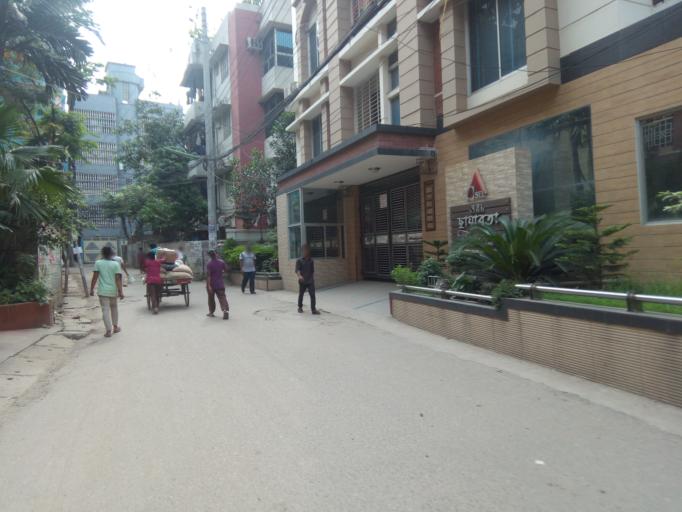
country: BD
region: Dhaka
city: Paltan
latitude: 23.7500
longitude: 90.4011
